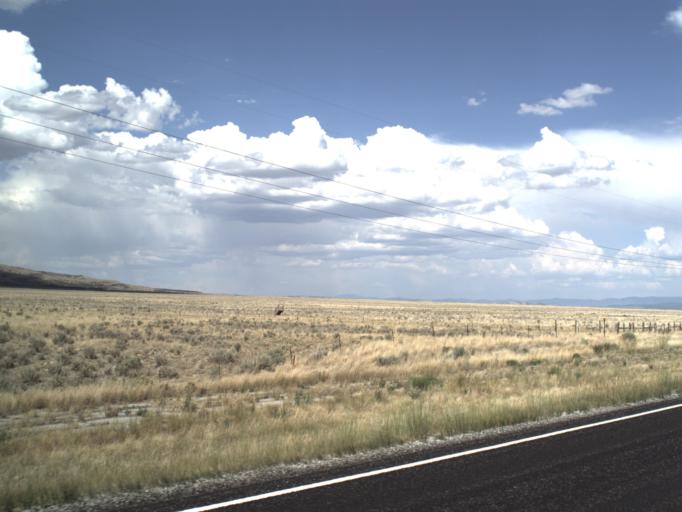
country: US
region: Idaho
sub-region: Minidoka County
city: Rupert
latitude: 41.9700
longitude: -113.1208
